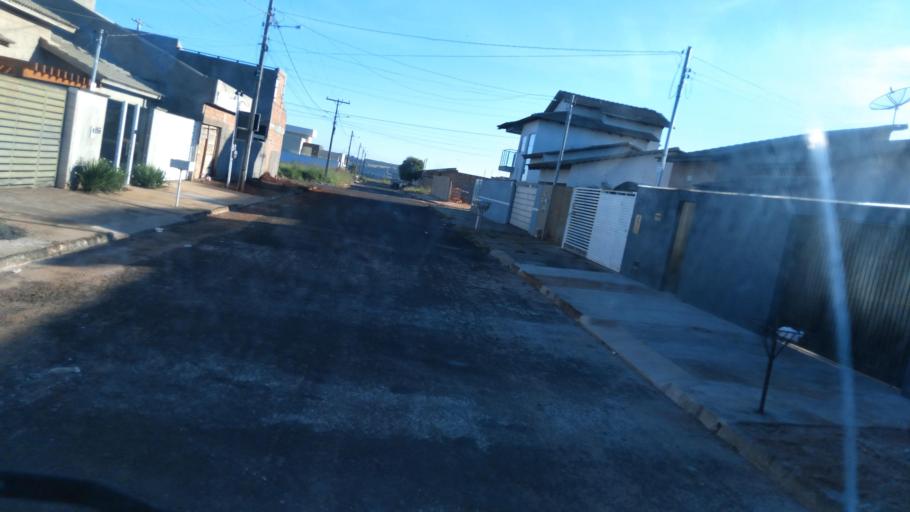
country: BR
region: Goias
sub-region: Mineiros
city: Mineiros
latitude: -17.5460
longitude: -52.5554
